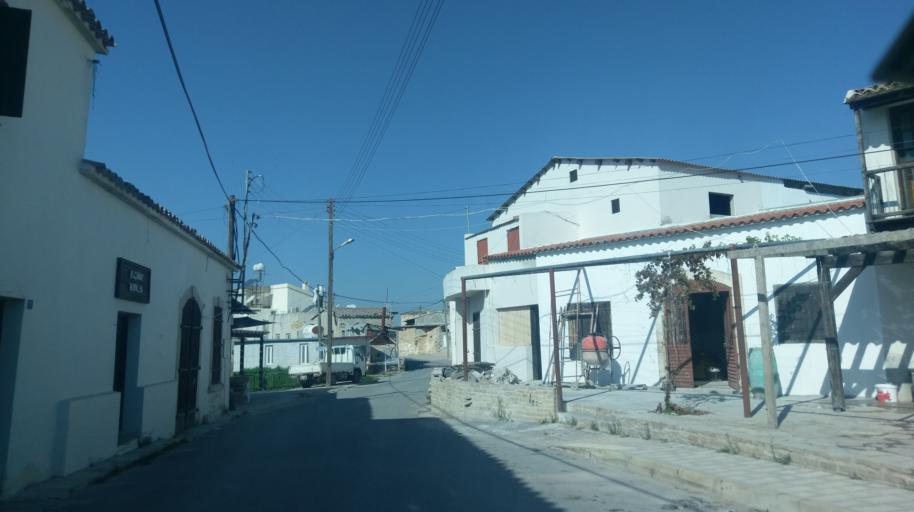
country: CY
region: Lefkosia
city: Lympia
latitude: 35.0113
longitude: 33.4650
